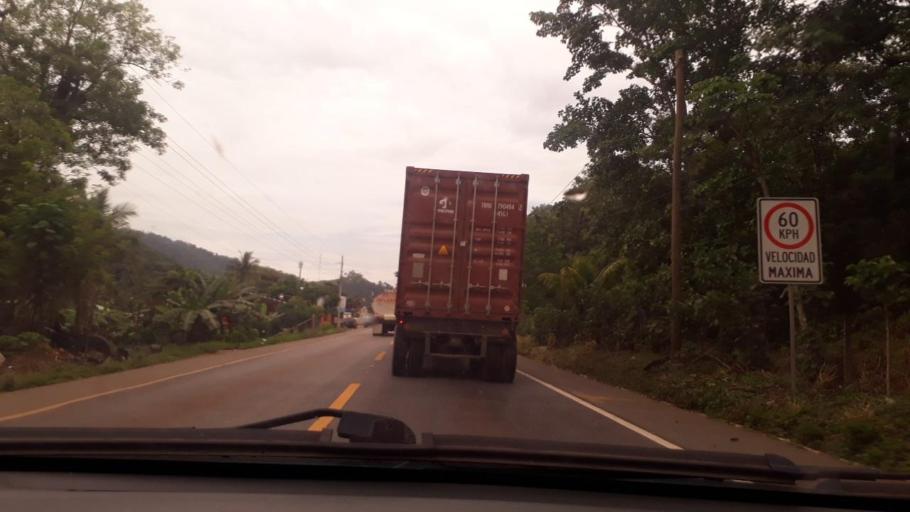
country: GT
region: Izabal
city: Morales
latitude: 15.5501
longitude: -88.6909
